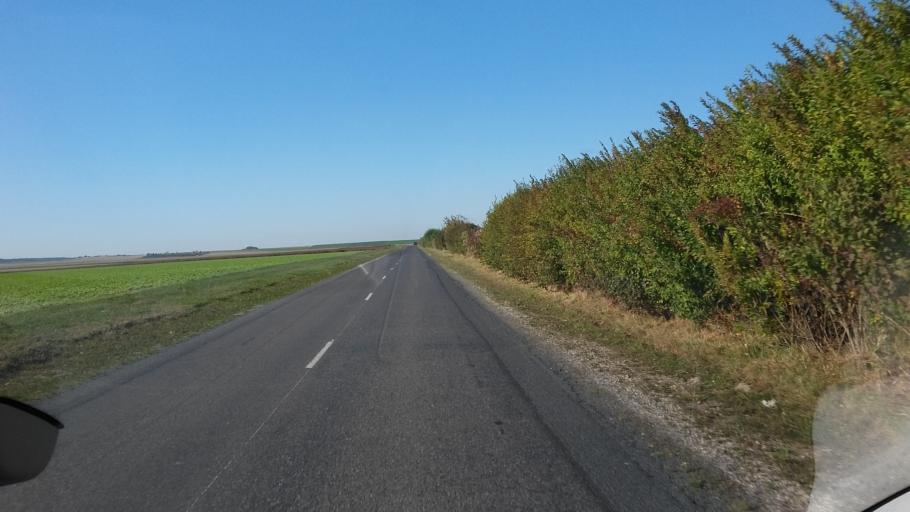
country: FR
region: Champagne-Ardenne
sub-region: Departement de la Marne
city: Connantre
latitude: 48.7415
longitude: 3.8953
